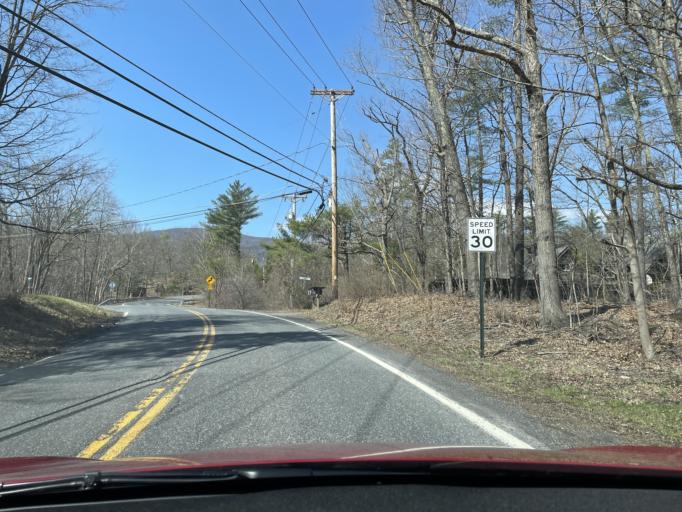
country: US
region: New York
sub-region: Ulster County
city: Manorville
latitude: 42.1051
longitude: -74.0206
